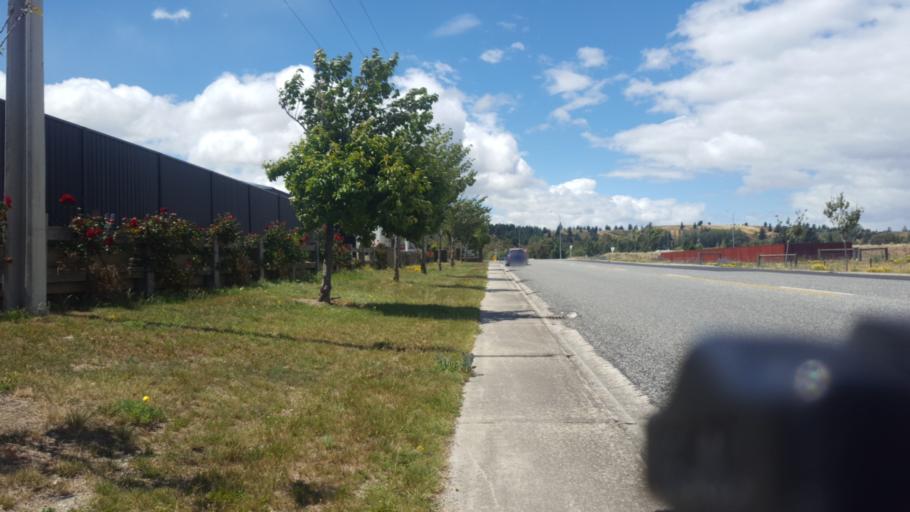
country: NZ
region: Otago
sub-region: Queenstown-Lakes District
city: Wanaka
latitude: -45.1980
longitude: 169.3346
